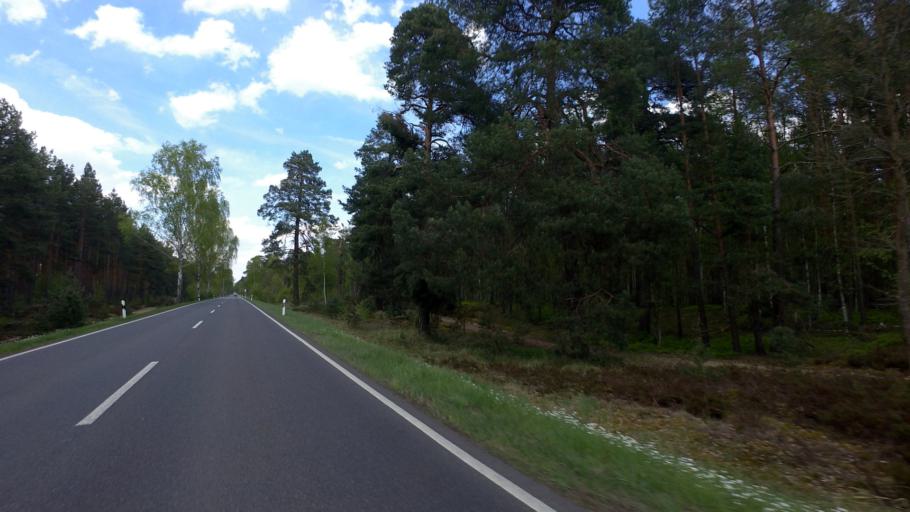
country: DE
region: Brandenburg
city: Marienwerder
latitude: 52.9669
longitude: 13.5736
